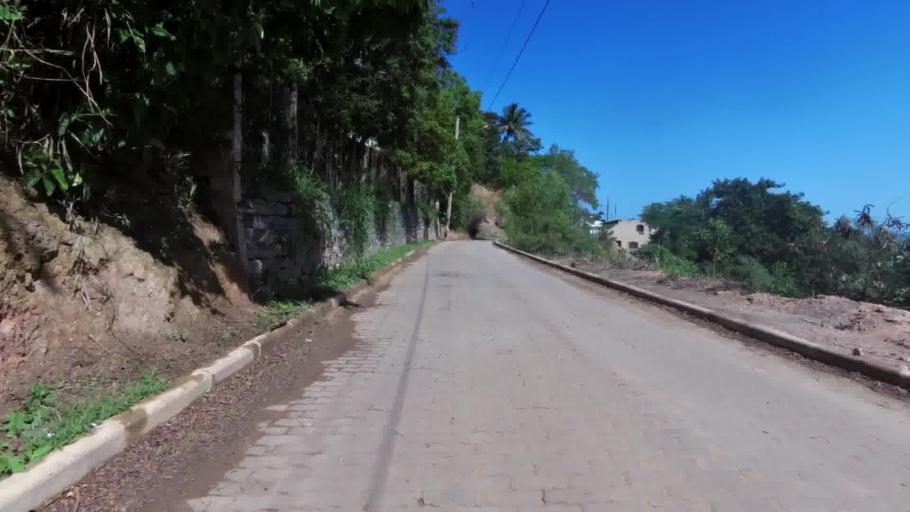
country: BR
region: Espirito Santo
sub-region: Piuma
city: Piuma
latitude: -20.8219
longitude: -40.6289
